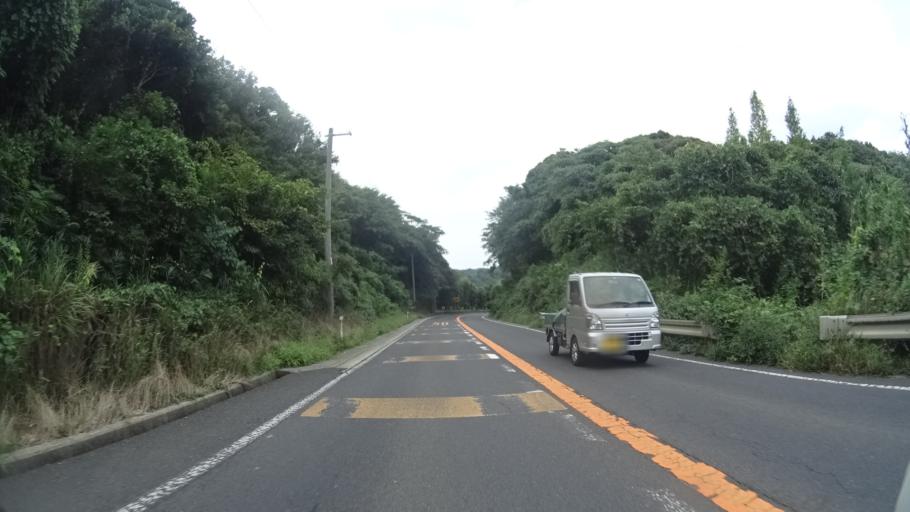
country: JP
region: Shimane
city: Odacho-oda
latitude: 35.1971
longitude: 132.4532
